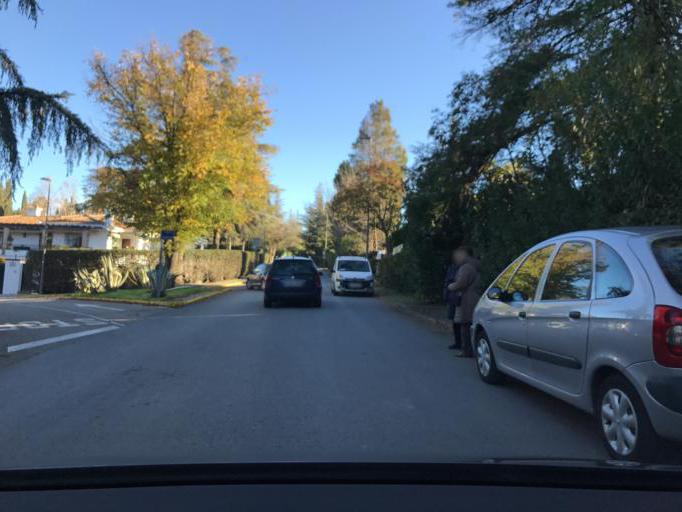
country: ES
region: Andalusia
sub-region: Provincia de Granada
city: Albolote
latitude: 37.2509
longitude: -3.6513
